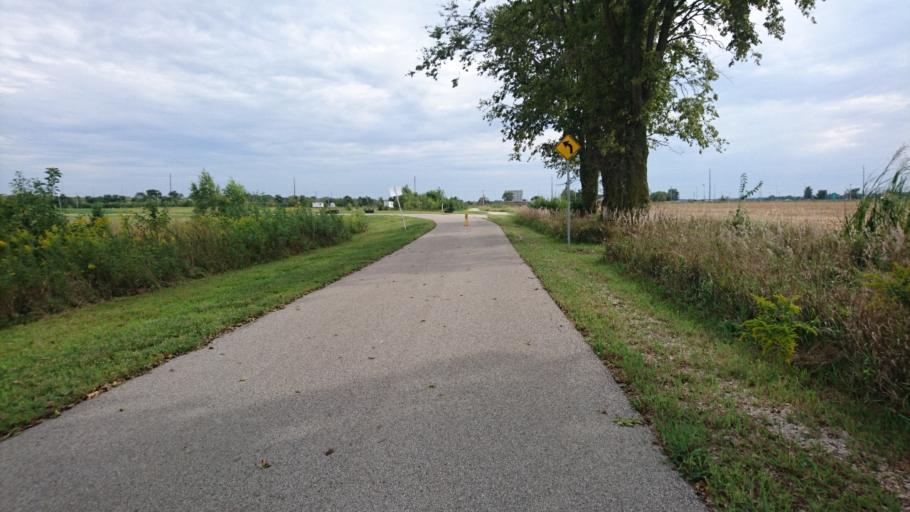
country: US
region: Illinois
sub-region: Sangamon County
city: Jerome
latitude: 39.7462
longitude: -89.6771
